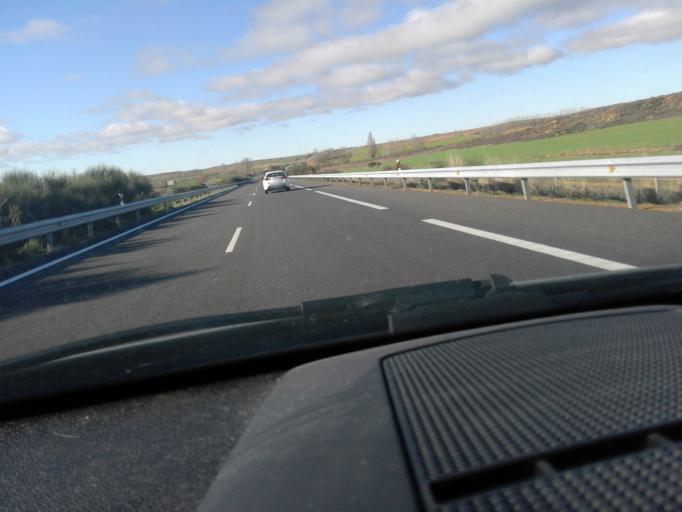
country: ES
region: Castille and Leon
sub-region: Provincia de Palencia
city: Ledigos
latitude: 42.3655
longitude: -4.8928
